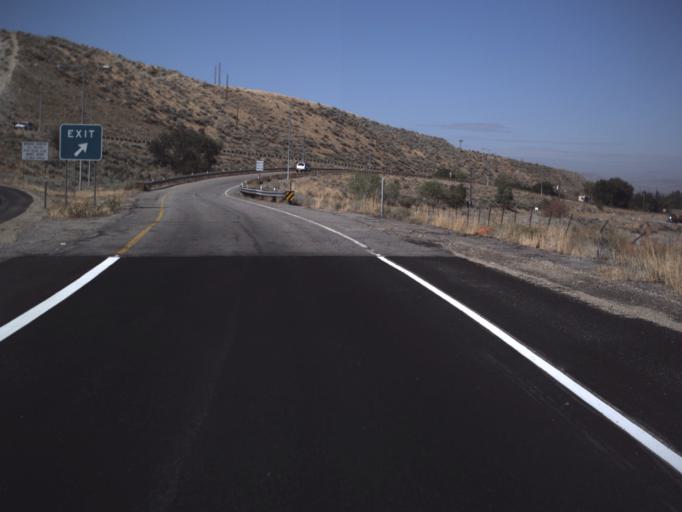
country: US
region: Utah
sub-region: Box Elder County
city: Brigham City
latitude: 41.4999
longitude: -111.9904
